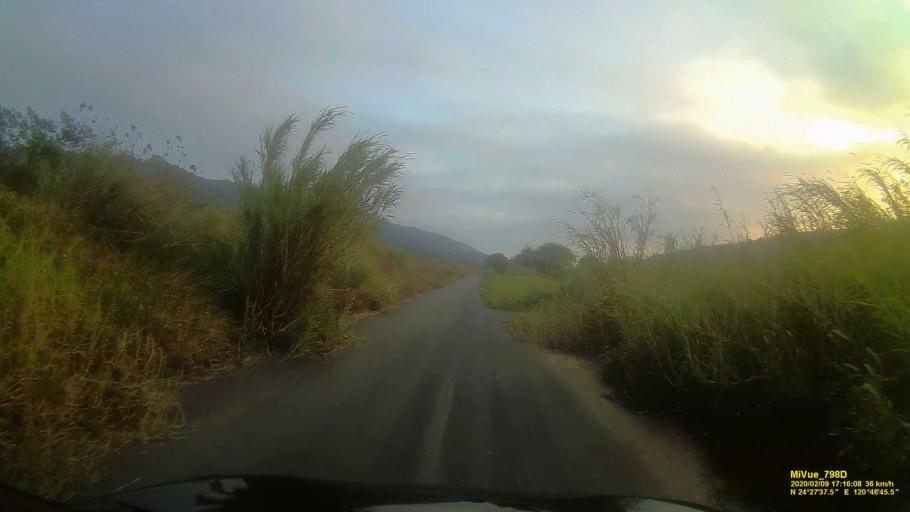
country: TW
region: Taiwan
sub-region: Miaoli
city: Miaoli
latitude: 24.4602
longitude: 120.7793
